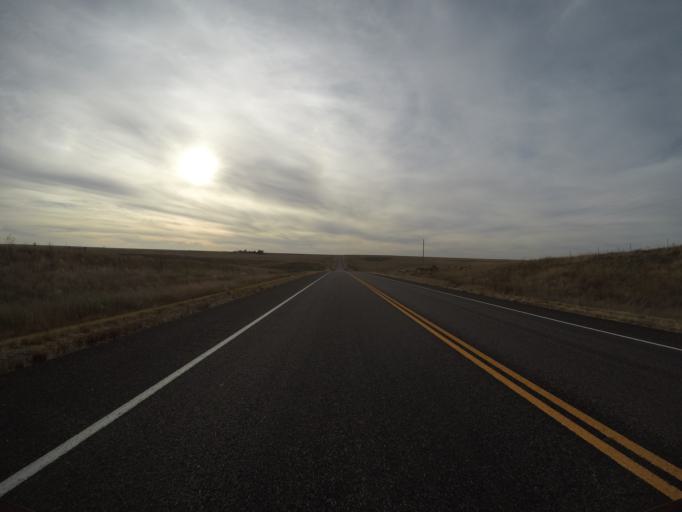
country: US
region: Kansas
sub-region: Cheyenne County
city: Saint Francis
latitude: 39.7467
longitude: -102.0779
